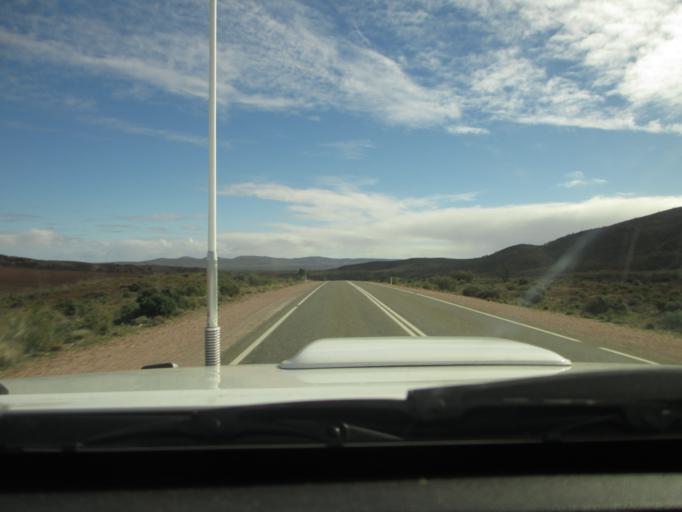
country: AU
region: South Australia
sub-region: Flinders Ranges
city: Quorn
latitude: -31.7963
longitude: 138.3583
